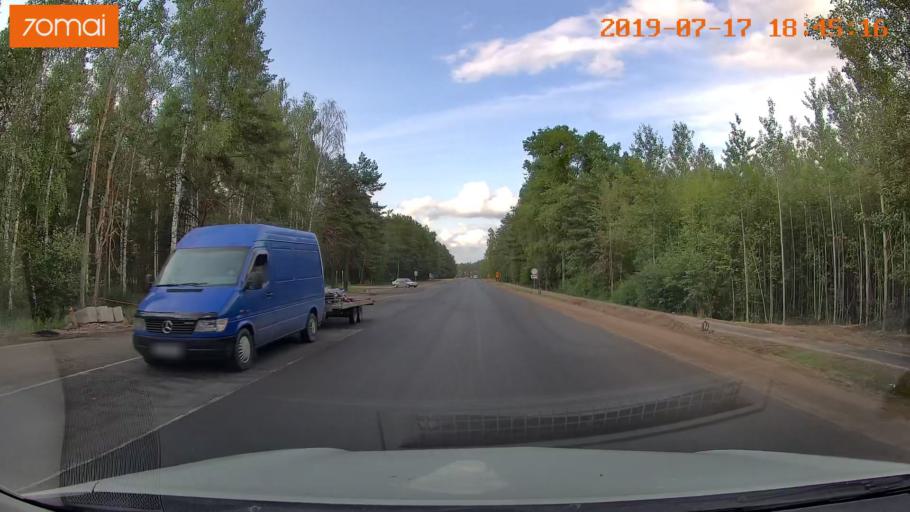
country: BY
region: Mogilev
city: Asipovichy
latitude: 53.3235
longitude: 28.6529
